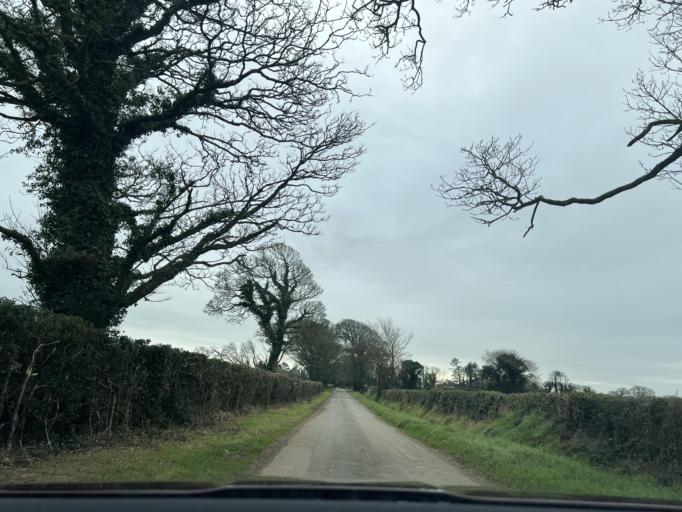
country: IE
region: Leinster
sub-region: Loch Garman
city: Castlebridge
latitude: 52.3886
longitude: -6.5327
